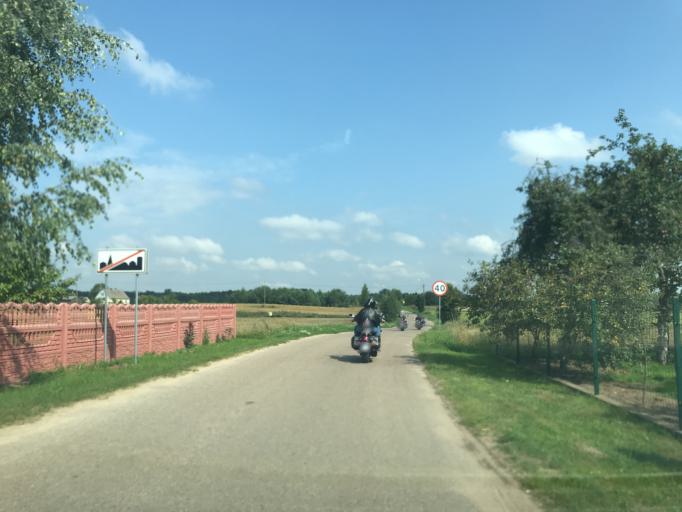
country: PL
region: Warmian-Masurian Voivodeship
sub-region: Powiat nowomiejski
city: Biskupiec
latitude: 53.4234
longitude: 19.4422
